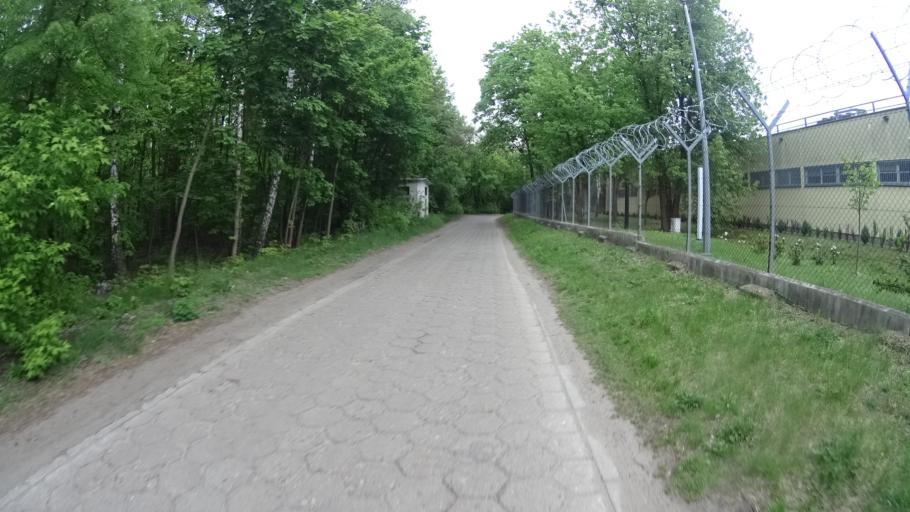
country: PL
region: Masovian Voivodeship
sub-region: Powiat warszawski zachodni
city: Babice
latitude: 52.2634
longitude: 20.8771
